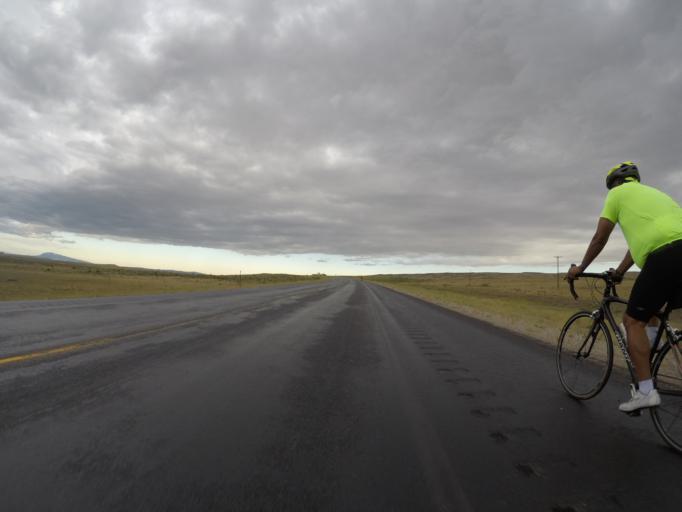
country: US
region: Wyoming
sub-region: Albany County
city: Laramie
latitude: 41.8634
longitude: -106.0650
